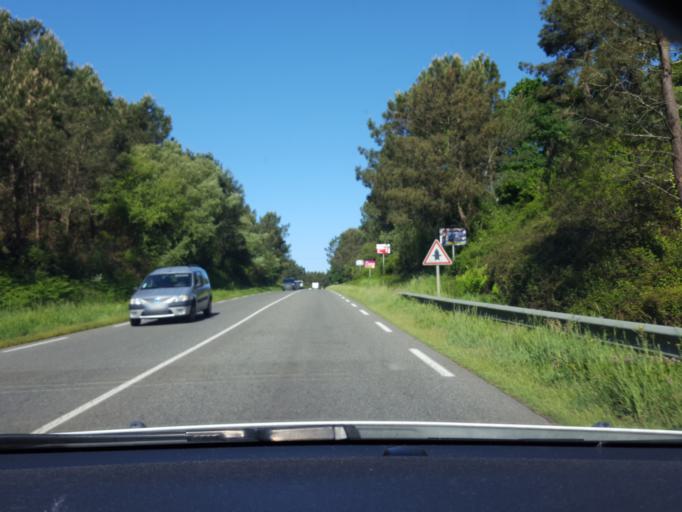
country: FR
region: Aquitaine
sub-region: Departement des Landes
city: Ondres
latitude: 43.5460
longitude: -1.4413
